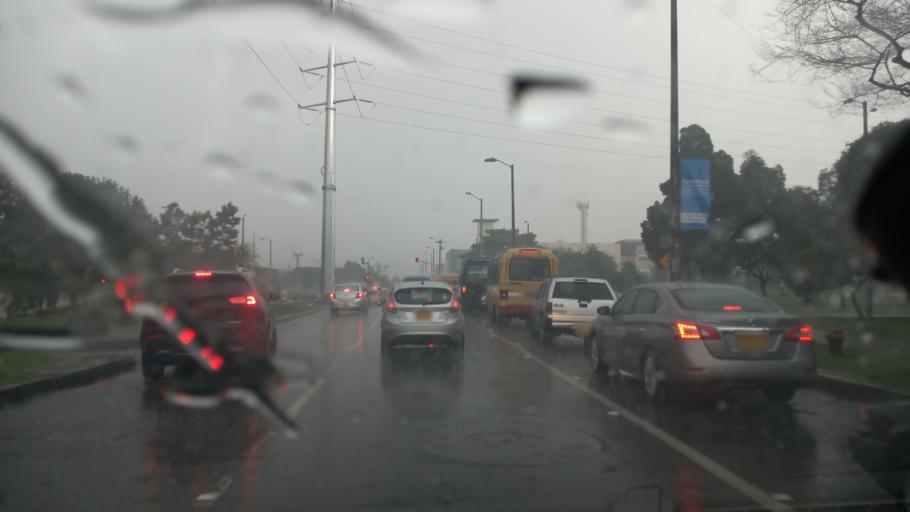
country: CO
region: Bogota D.C.
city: Bogota
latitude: 4.6666
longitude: -74.1314
